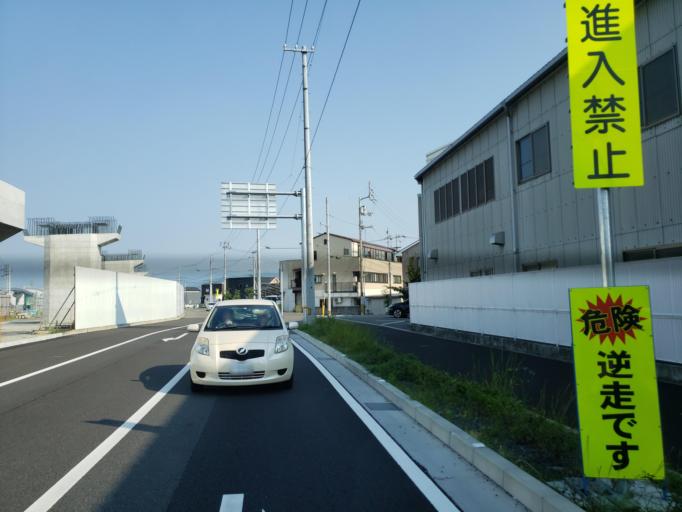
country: JP
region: Ehime
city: Masaki-cho
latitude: 33.8211
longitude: 132.7141
